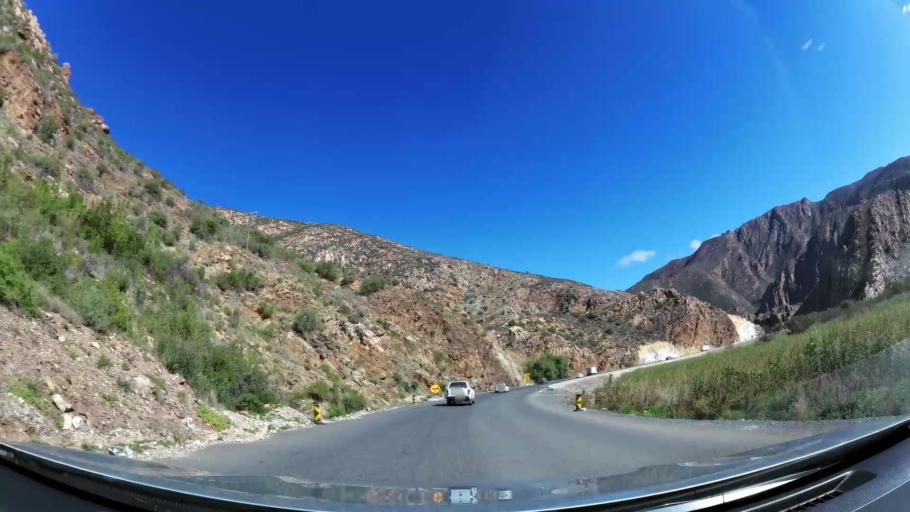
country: ZA
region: Western Cape
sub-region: Cape Winelands District Municipality
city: Ashton
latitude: -33.8035
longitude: 20.1038
